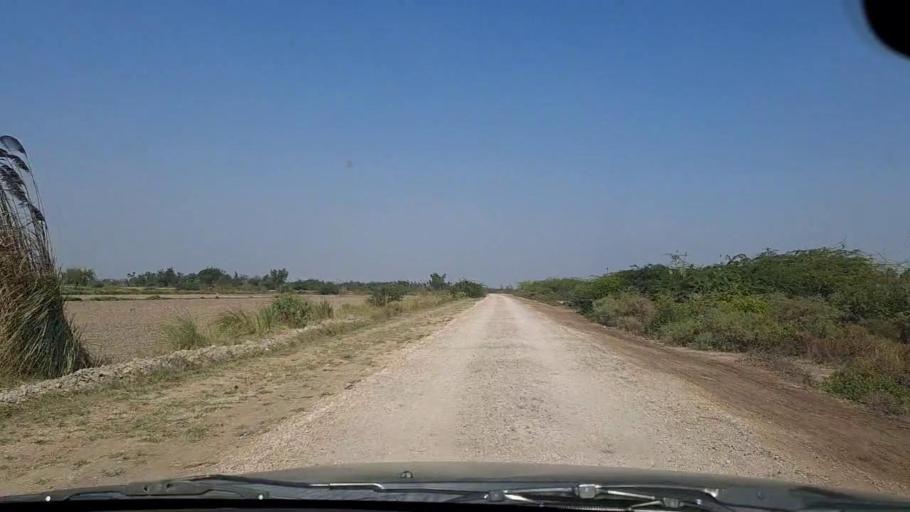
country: PK
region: Sindh
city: Chuhar Jamali
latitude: 24.4382
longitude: 67.7992
